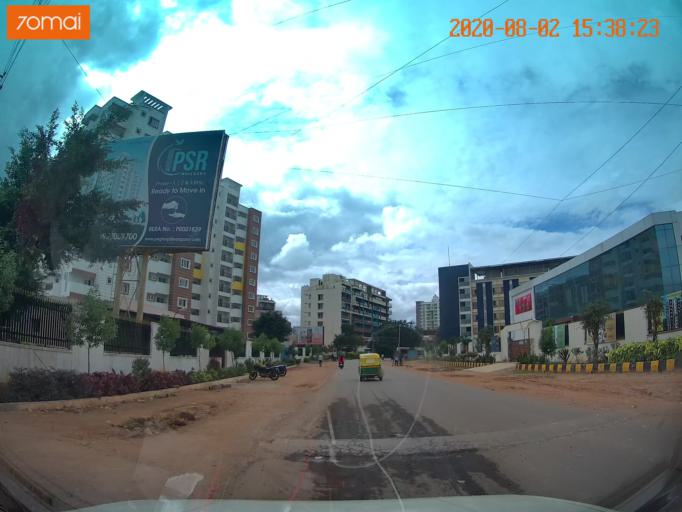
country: IN
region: Karnataka
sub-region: Bangalore Urban
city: Anekal
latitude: 12.8399
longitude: 77.6444
